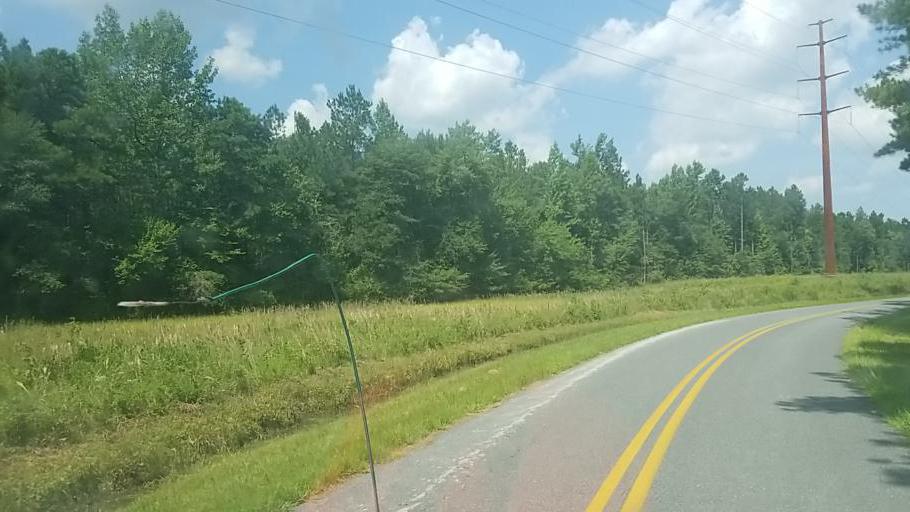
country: US
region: Maryland
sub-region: Worcester County
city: Snow Hill
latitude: 38.2768
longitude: -75.4744
